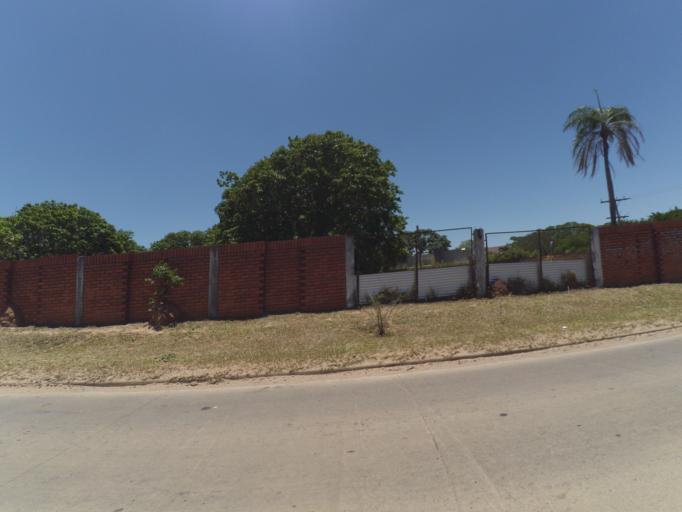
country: BO
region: Santa Cruz
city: Santa Cruz de la Sierra
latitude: -17.7597
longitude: -63.2219
